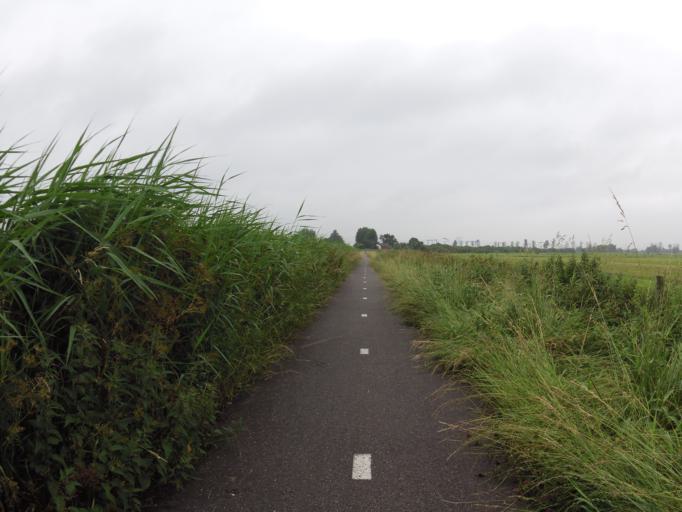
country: NL
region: Utrecht
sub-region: Stichtse Vecht
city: Spechtenkamp
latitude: 52.1200
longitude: 4.9722
